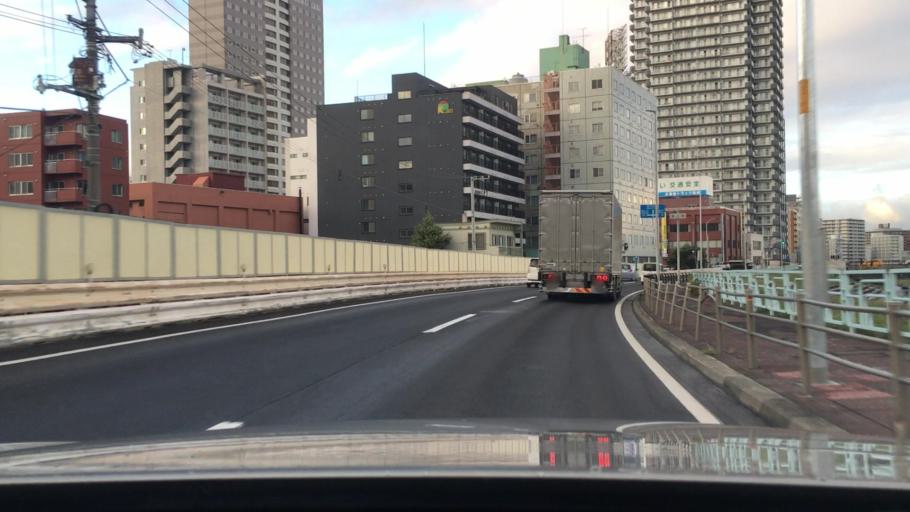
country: JP
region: Hokkaido
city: Sapporo
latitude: 43.0475
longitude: 141.3580
